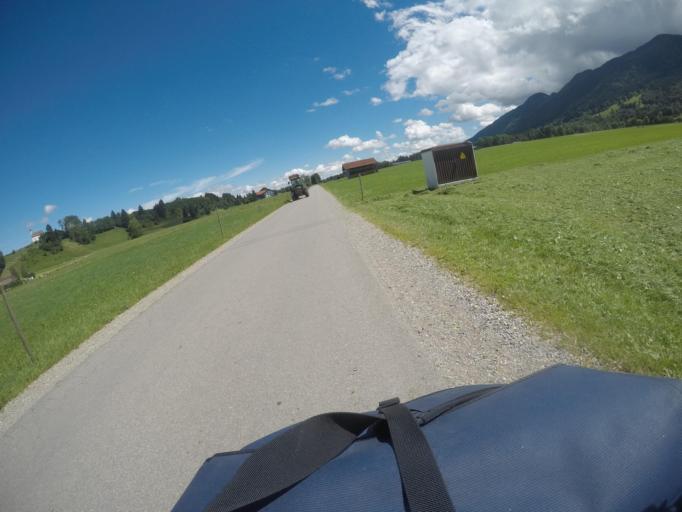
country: DE
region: Bavaria
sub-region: Swabia
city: Halblech
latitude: 47.6258
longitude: 10.8062
